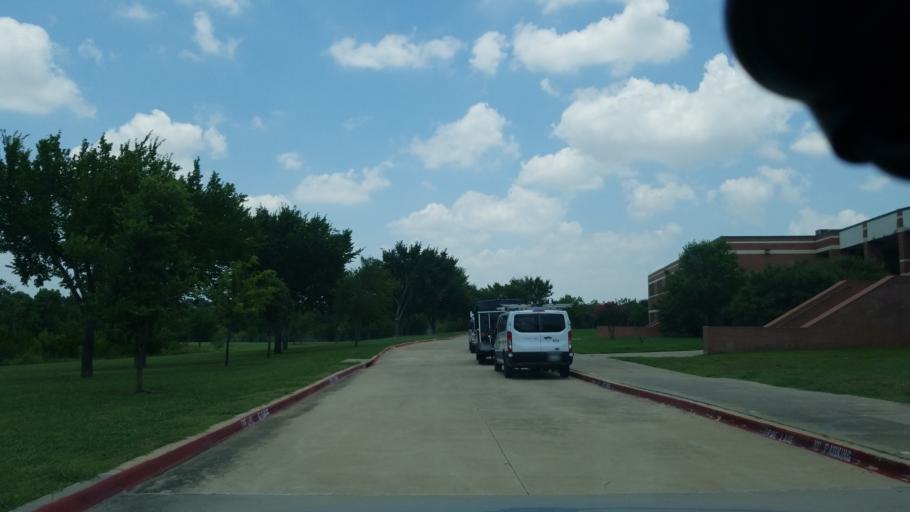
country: US
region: Texas
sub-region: Dallas County
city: Carrollton
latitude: 32.9645
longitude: -96.8800
